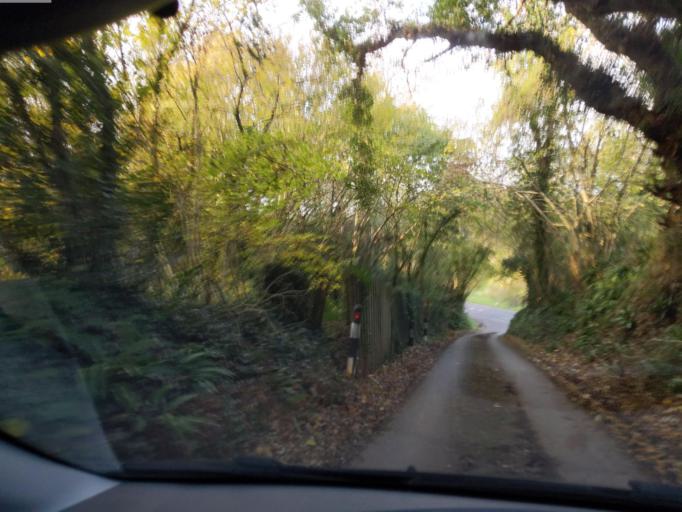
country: GB
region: England
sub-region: Cornwall
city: Wadebridge
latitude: 50.5077
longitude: -4.8025
